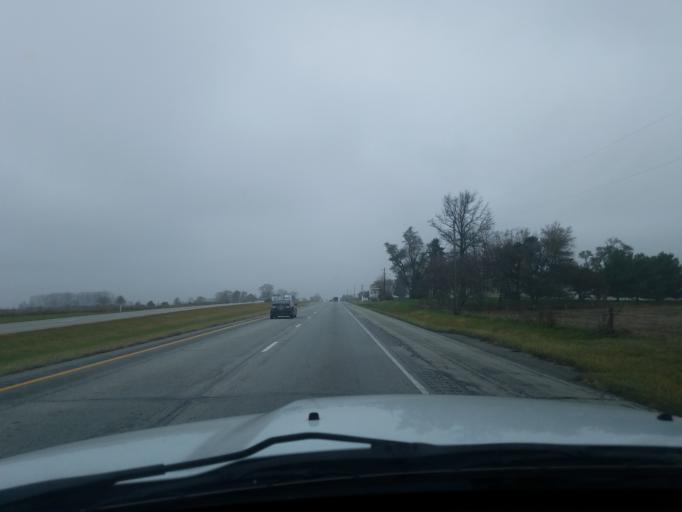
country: US
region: Indiana
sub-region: Hamilton County
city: Arcadia
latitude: 40.2026
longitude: -86.1279
